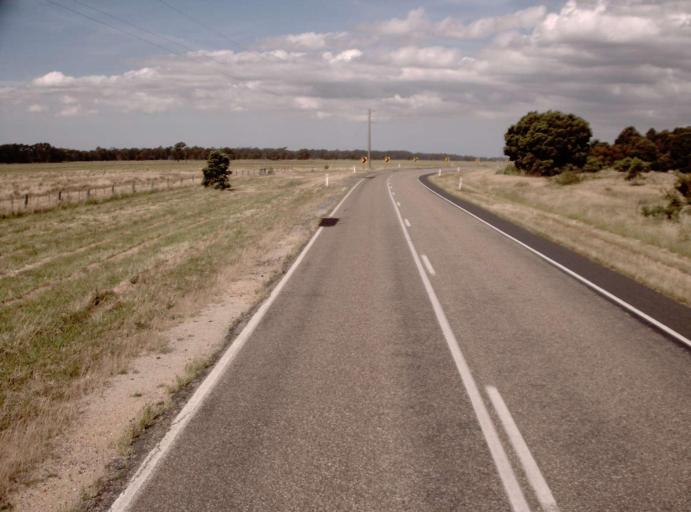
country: AU
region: Victoria
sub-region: Wellington
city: Sale
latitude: -38.1596
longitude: 146.9203
